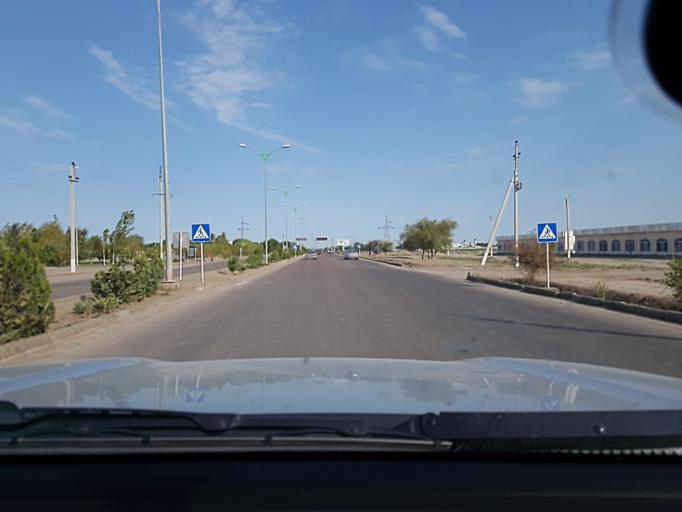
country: TM
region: Dasoguz
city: Koeneuergench
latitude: 42.3160
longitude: 59.1689
